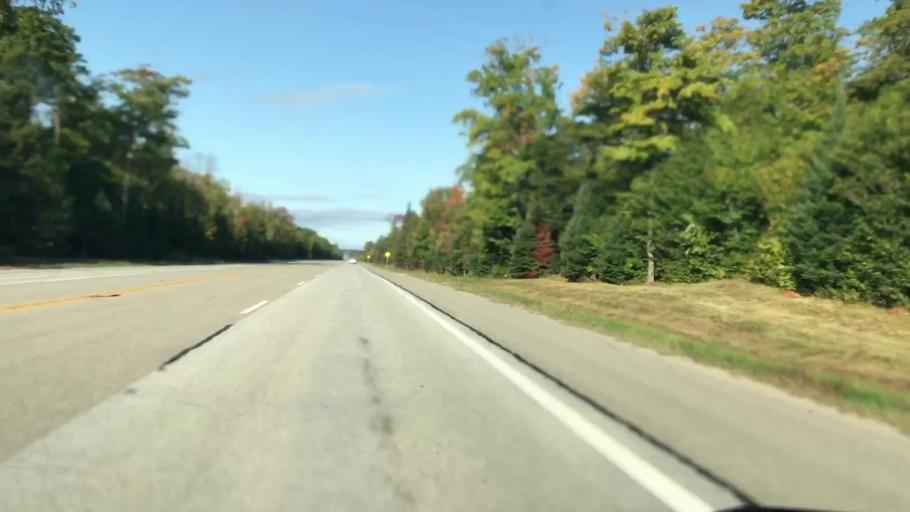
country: US
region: Michigan
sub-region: Luce County
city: Newberry
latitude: 46.3037
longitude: -85.2854
